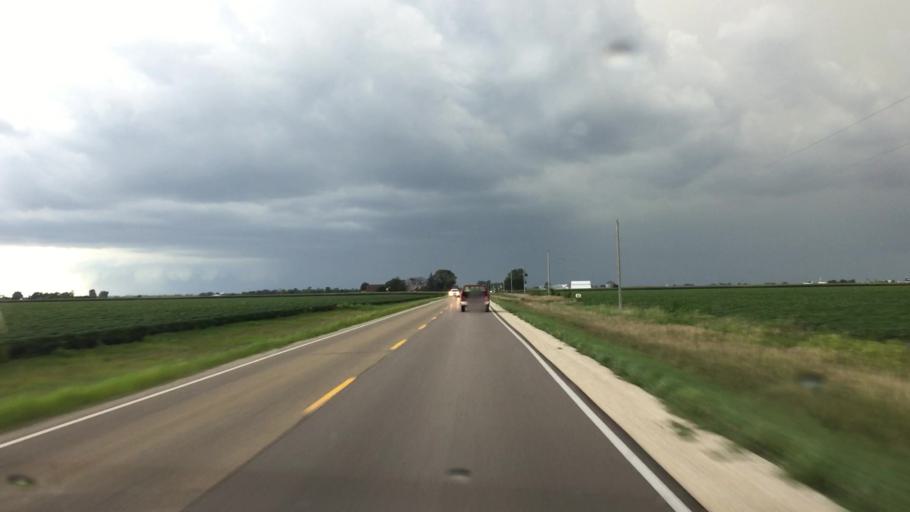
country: US
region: Iowa
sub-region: Henry County
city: New London
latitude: 40.7843
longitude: -91.4861
